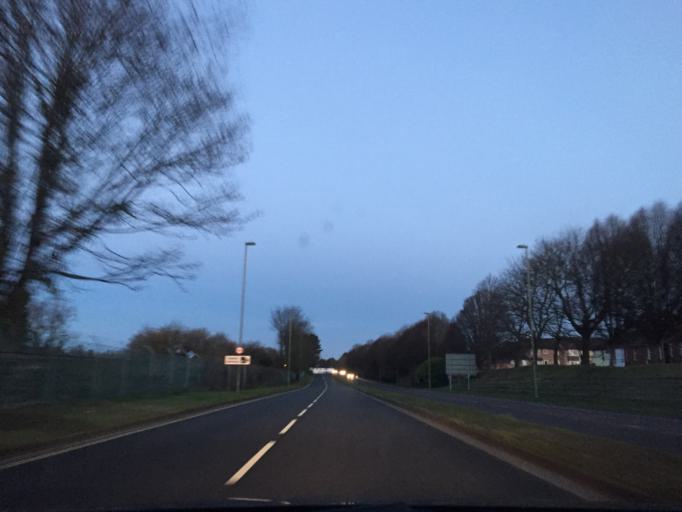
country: GB
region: England
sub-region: Hampshire
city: Fareham
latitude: 50.8509
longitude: -1.1820
